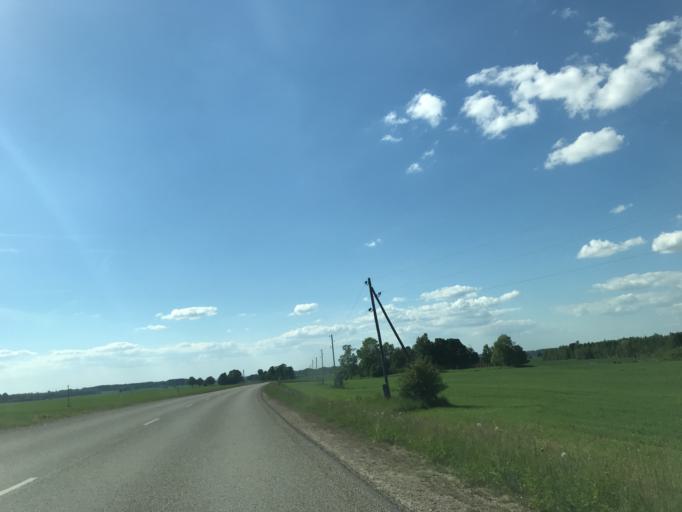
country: LV
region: Aizkraukles Rajons
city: Aizkraukle
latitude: 56.5709
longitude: 25.3180
